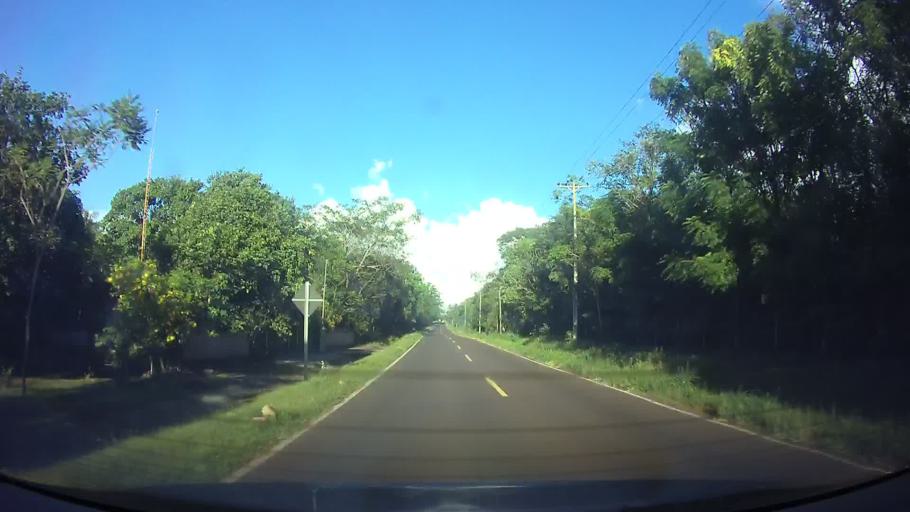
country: PY
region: Cordillera
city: Emboscada
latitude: -25.2027
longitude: -57.3335
